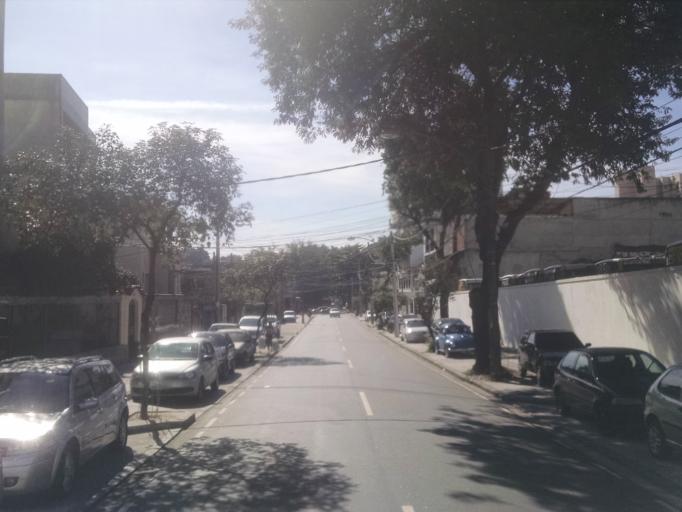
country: BR
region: Rio de Janeiro
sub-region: Rio De Janeiro
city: Rio de Janeiro
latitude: -22.9107
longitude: -43.2709
